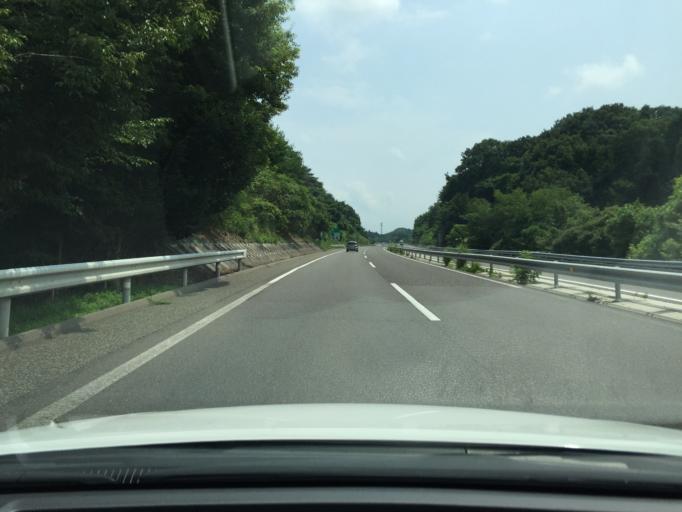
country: JP
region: Fukushima
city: Miharu
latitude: 37.4344
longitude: 140.4723
